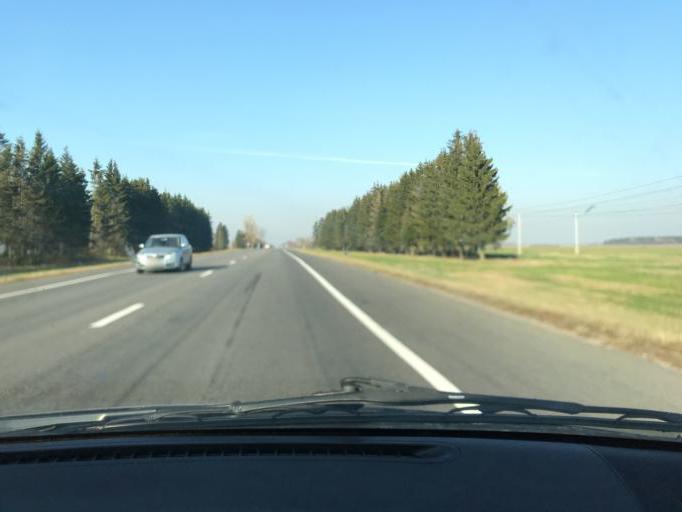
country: BY
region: Mogilev
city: Shklow
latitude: 54.2645
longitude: 30.4501
